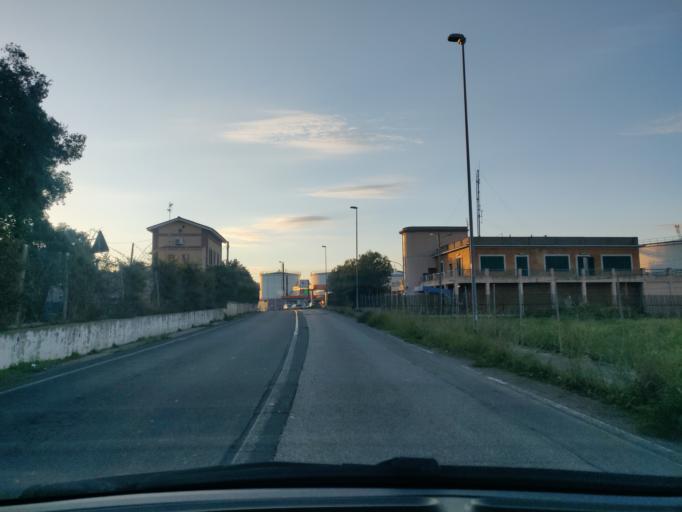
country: IT
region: Latium
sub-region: Citta metropolitana di Roma Capitale
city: Civitavecchia
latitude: 42.1093
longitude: 11.7780
